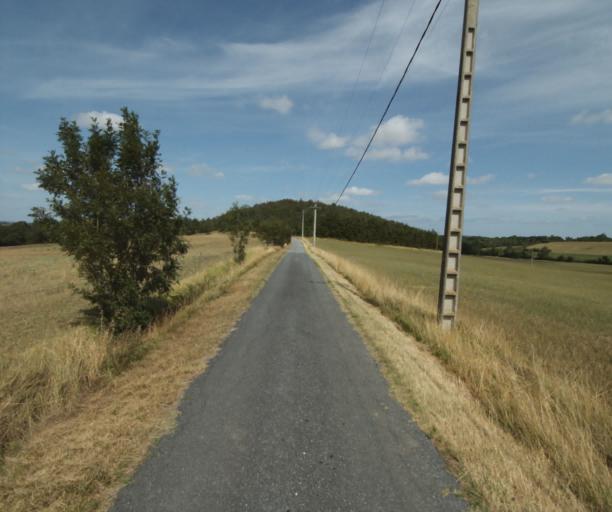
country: FR
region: Midi-Pyrenees
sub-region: Departement du Tarn
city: Dourgne
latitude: 43.4744
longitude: 2.1142
